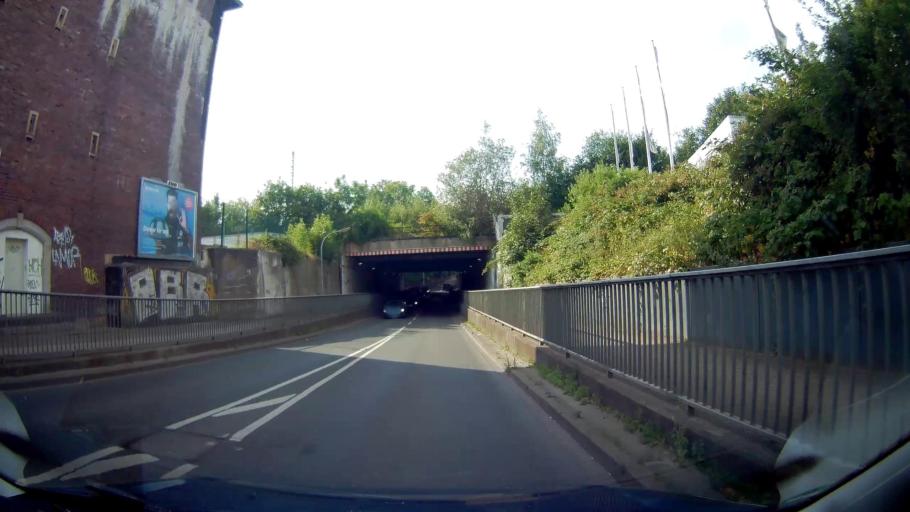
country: DE
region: North Rhine-Westphalia
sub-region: Regierungsbezirk Arnsberg
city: Herne
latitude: 51.5441
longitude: 7.2238
